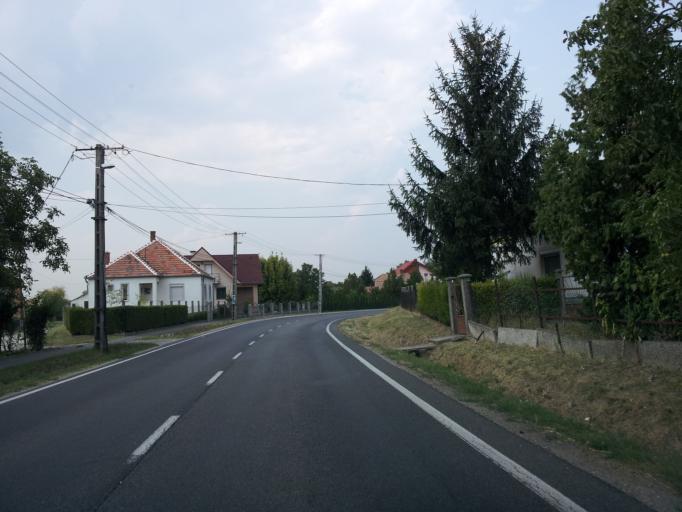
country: HU
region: Gyor-Moson-Sopron
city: Nyul
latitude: 47.5847
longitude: 17.6944
